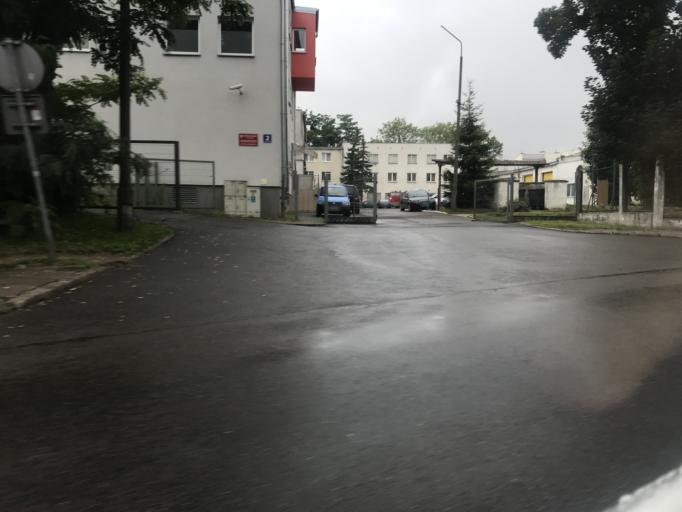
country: PL
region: Warmian-Masurian Voivodeship
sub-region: Powiat elblaski
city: Elblag
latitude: 54.1600
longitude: 19.4176
